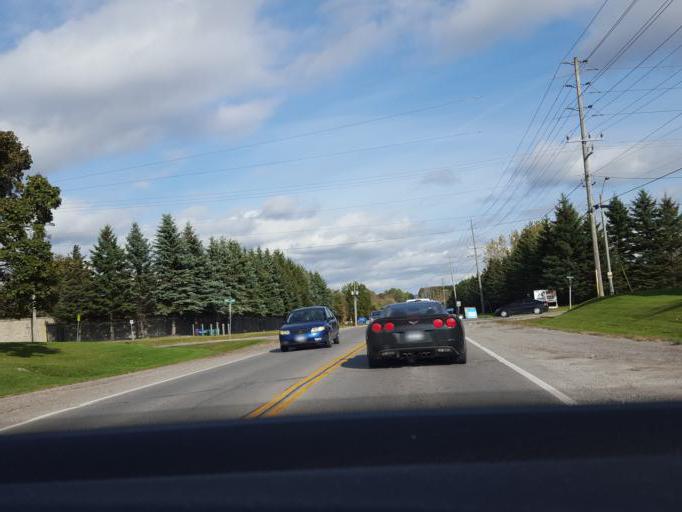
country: CA
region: Ontario
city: Oshawa
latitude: 43.9642
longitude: -78.7434
